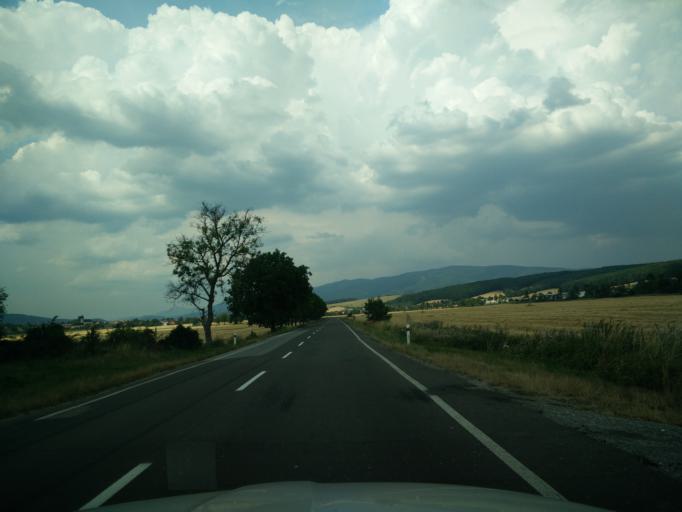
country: SK
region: Nitriansky
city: Novaky
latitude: 48.7531
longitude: 18.4973
